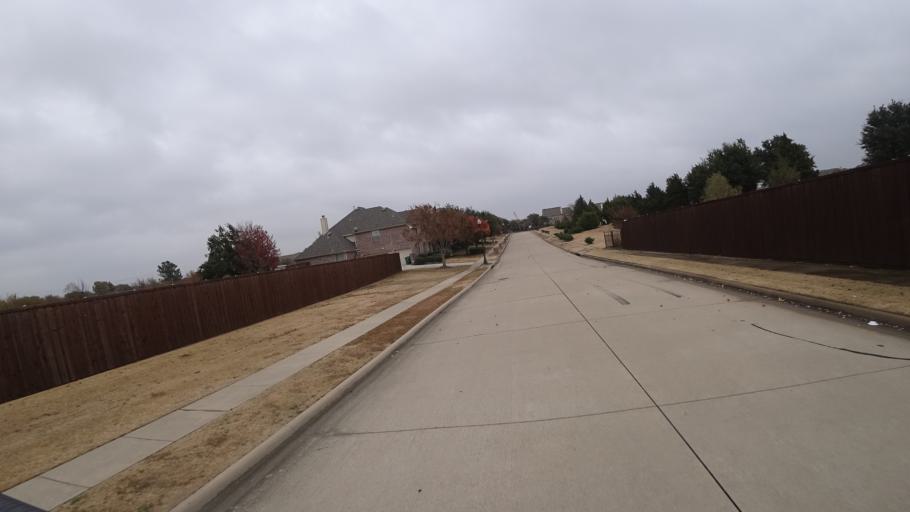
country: US
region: Texas
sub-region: Denton County
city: Lewisville
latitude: 33.0384
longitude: -96.9349
